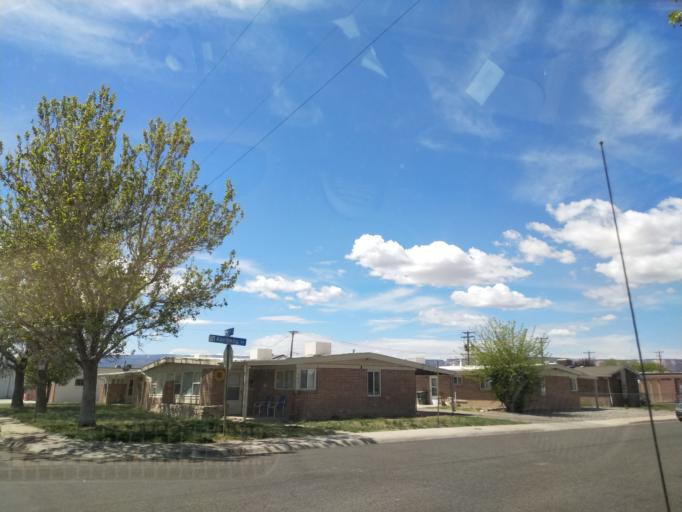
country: US
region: Colorado
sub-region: Mesa County
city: Grand Junction
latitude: 39.0800
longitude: -108.5645
